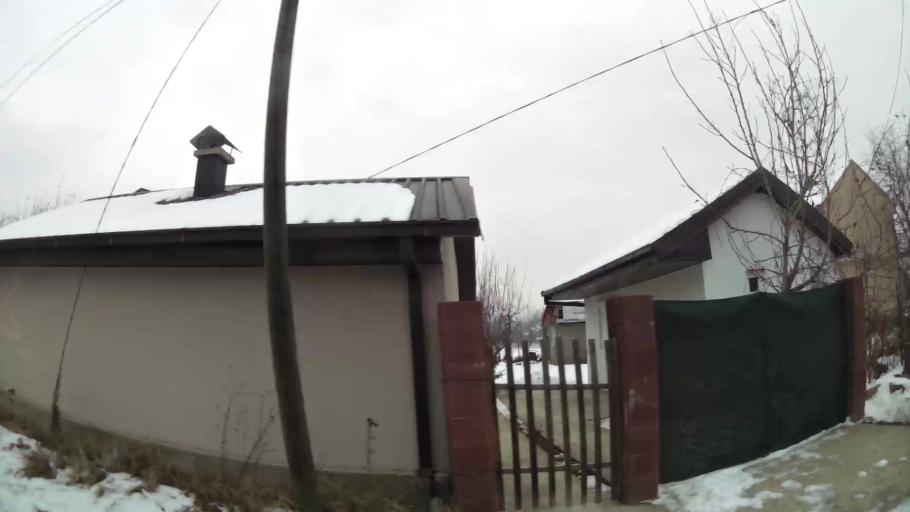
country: MK
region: Cucer-Sandevo
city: Chucher - Sandevo
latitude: 42.0498
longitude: 21.3593
